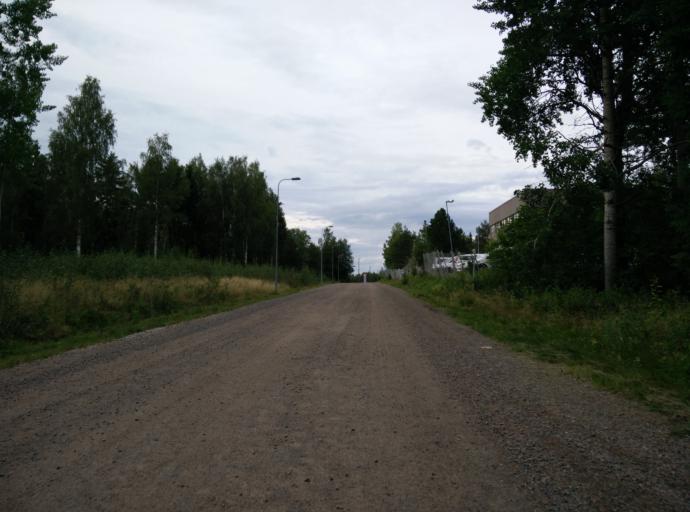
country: FI
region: Haeme
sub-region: Haemeenlinna
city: Haemeenlinna
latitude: 60.9866
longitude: 24.4806
